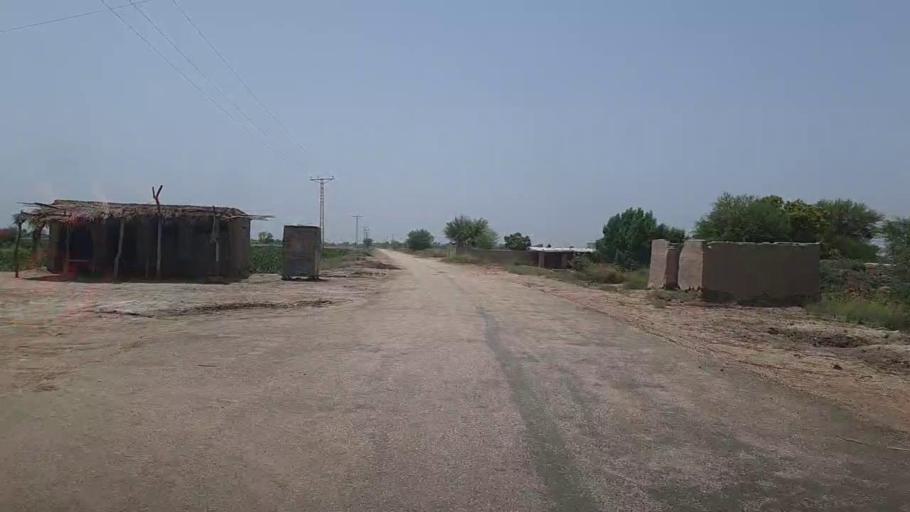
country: PK
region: Sindh
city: Pad Idan
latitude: 26.8343
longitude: 68.3230
